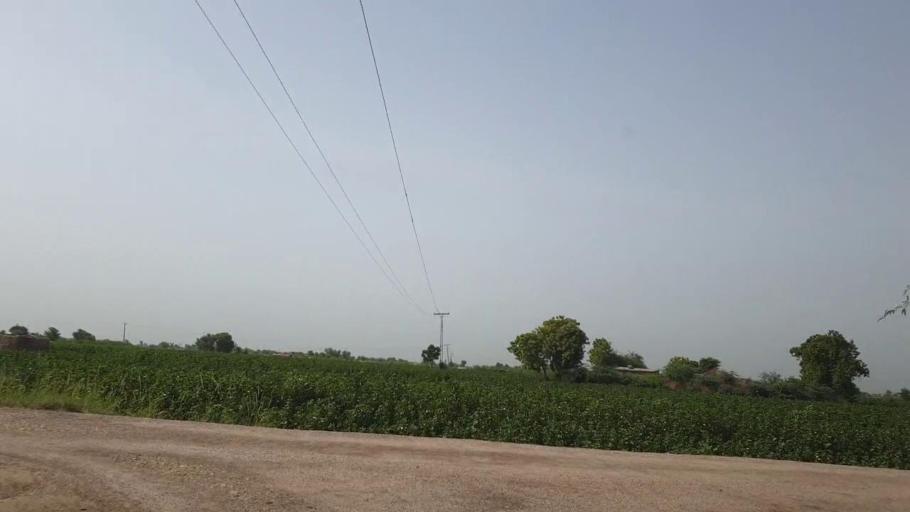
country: PK
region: Sindh
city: Nawabshah
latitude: 26.1093
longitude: 68.4438
